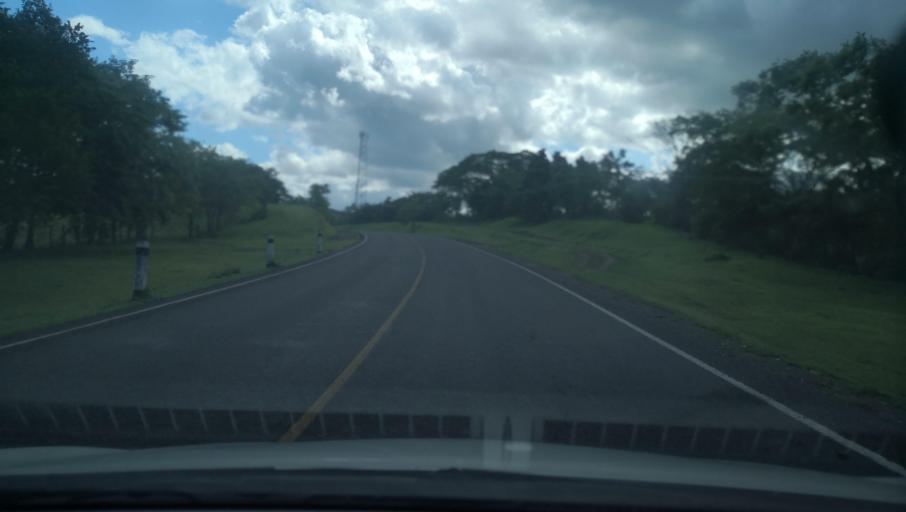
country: NI
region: Madriz
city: Somoto
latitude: 13.4674
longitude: -86.6518
